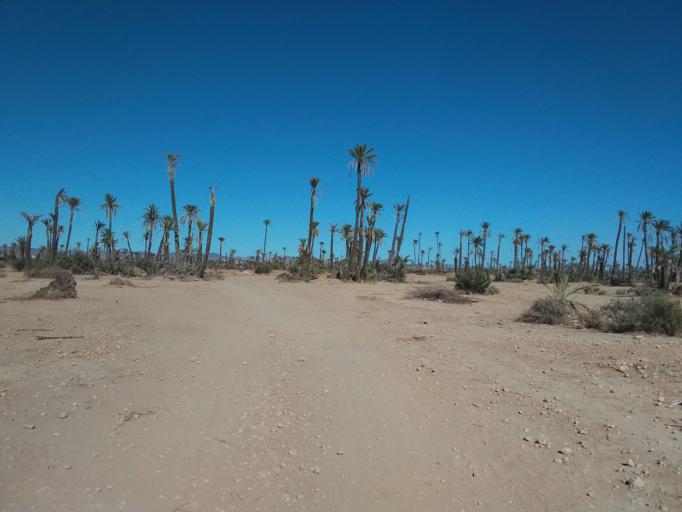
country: MA
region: Marrakech-Tensift-Al Haouz
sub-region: Marrakech
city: Marrakesh
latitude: 31.6789
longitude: -7.9518
